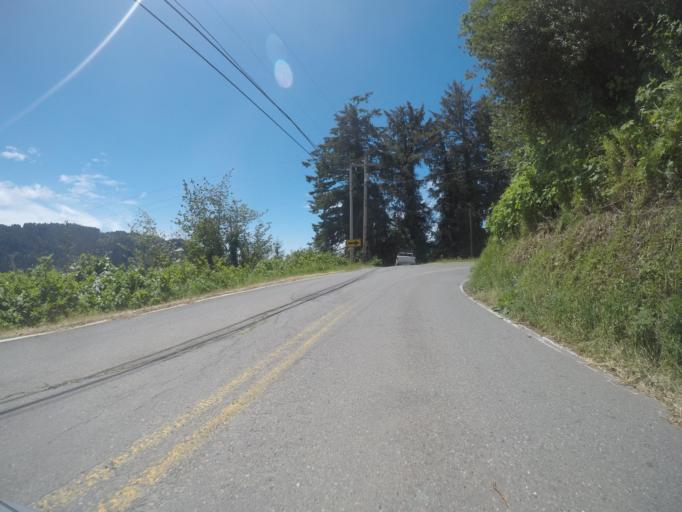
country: US
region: California
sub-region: Del Norte County
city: Bertsch-Oceanview
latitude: 41.5473
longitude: -124.0739
